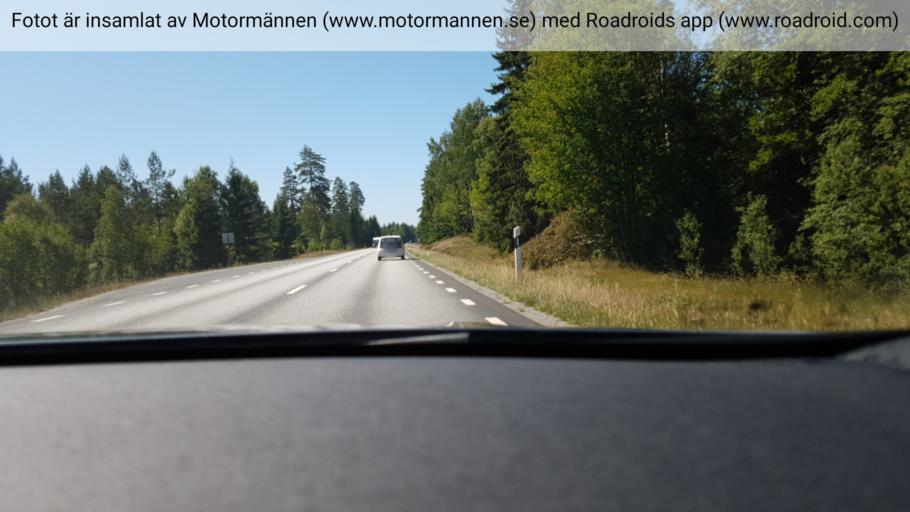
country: SE
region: Joenkoeping
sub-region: Gnosjo Kommun
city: Gnosjoe
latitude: 57.5876
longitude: 13.7274
